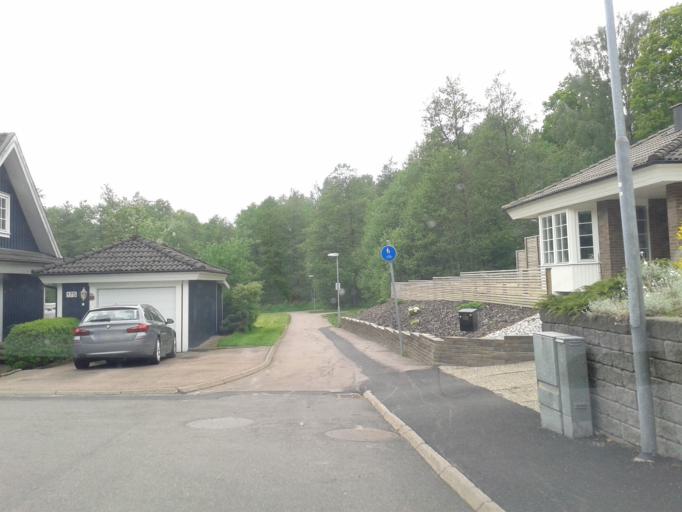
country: SE
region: Vaestra Goetaland
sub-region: Kungalvs Kommun
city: Kungalv
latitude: 57.8823
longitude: 11.9566
